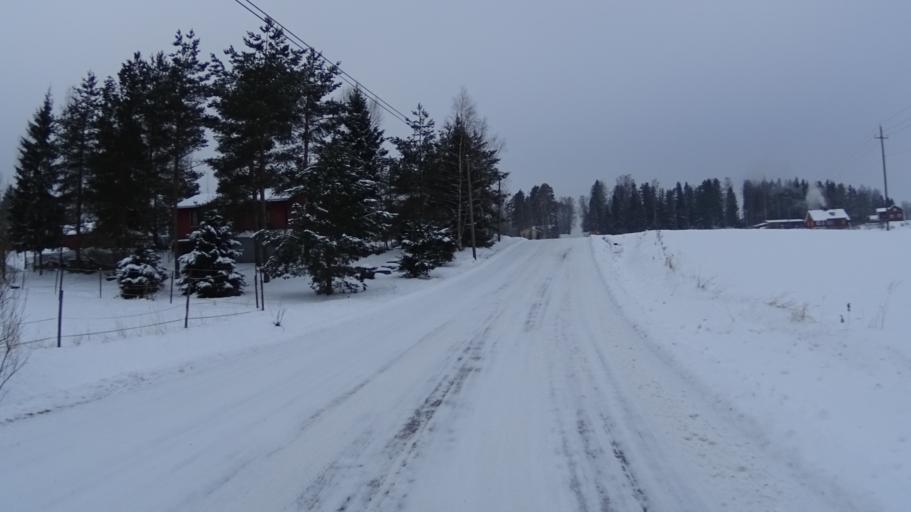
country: FI
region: Uusimaa
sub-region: Helsinki
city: Vihti
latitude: 60.3487
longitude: 24.2111
